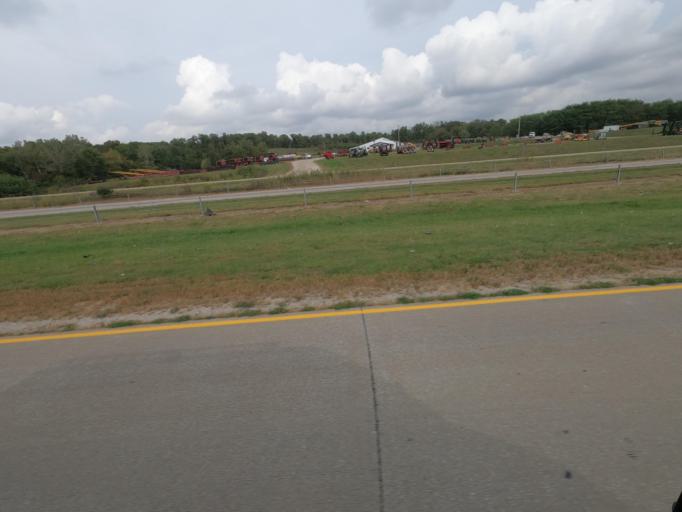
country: US
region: Iowa
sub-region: Wapello County
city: Ottumwa
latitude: 41.0094
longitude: -92.3702
